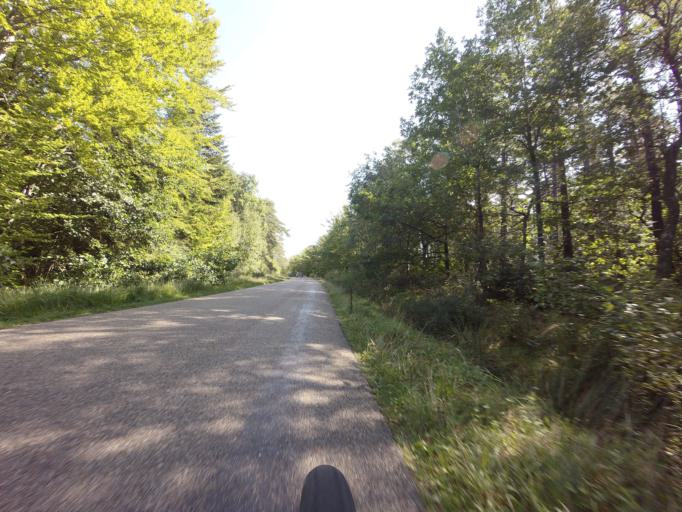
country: DK
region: North Denmark
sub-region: Hjorring Kommune
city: Hirtshals
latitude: 57.5829
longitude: 9.9977
